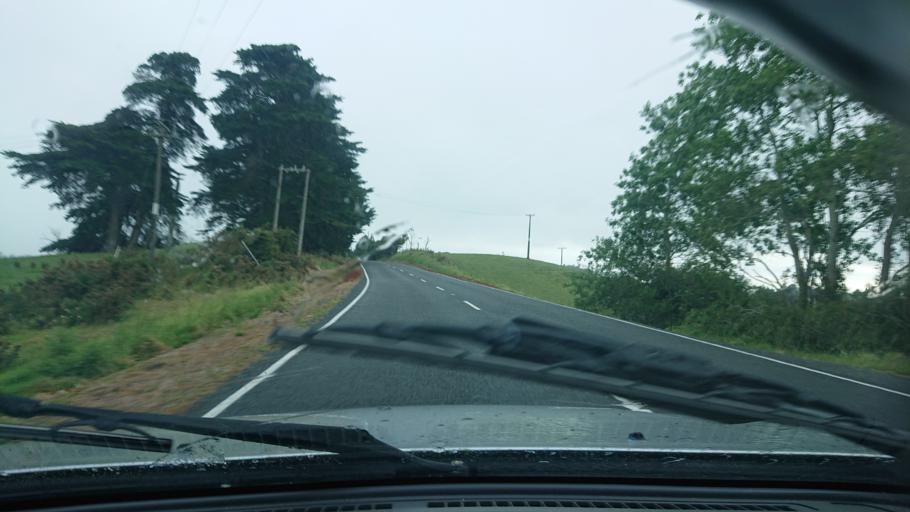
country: NZ
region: Auckland
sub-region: Auckland
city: Wellsford
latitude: -36.3353
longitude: 174.4001
